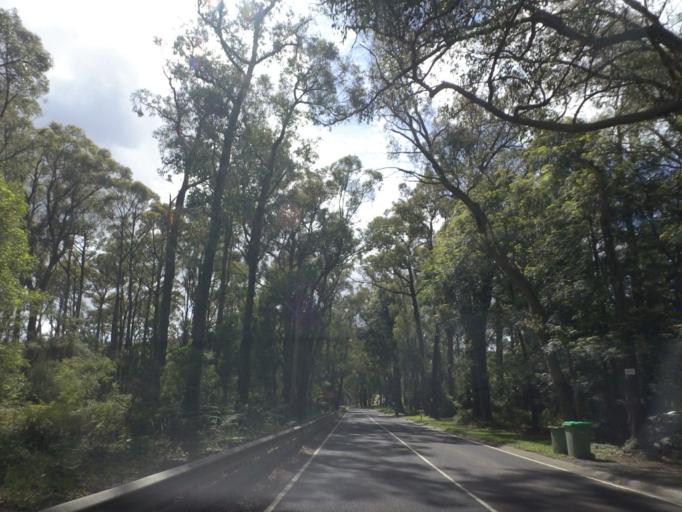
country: AU
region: Victoria
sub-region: Cardinia
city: Emerald
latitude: -37.9238
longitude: 145.4608
